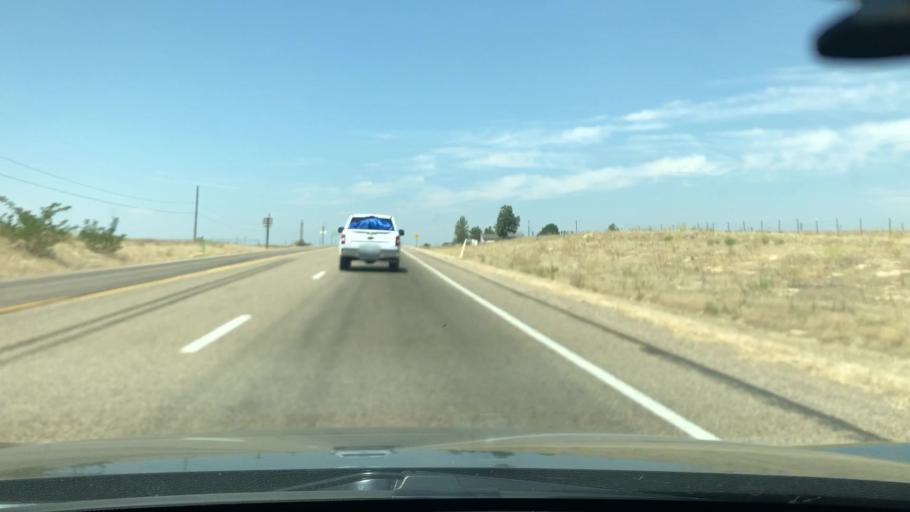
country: US
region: Idaho
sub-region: Canyon County
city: Parma
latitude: 43.8223
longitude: -116.9545
